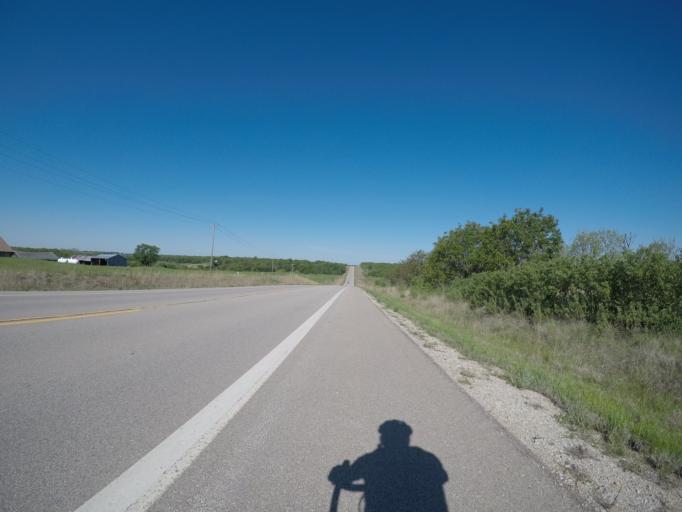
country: US
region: Kansas
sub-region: Douglas County
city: Lawrence
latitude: 38.9713
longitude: -95.4285
